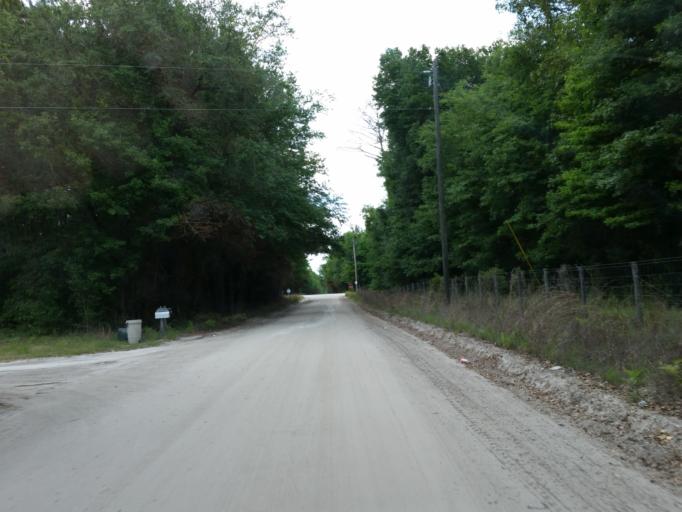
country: US
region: Florida
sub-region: Alachua County
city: High Springs
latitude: 29.9516
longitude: -82.5764
